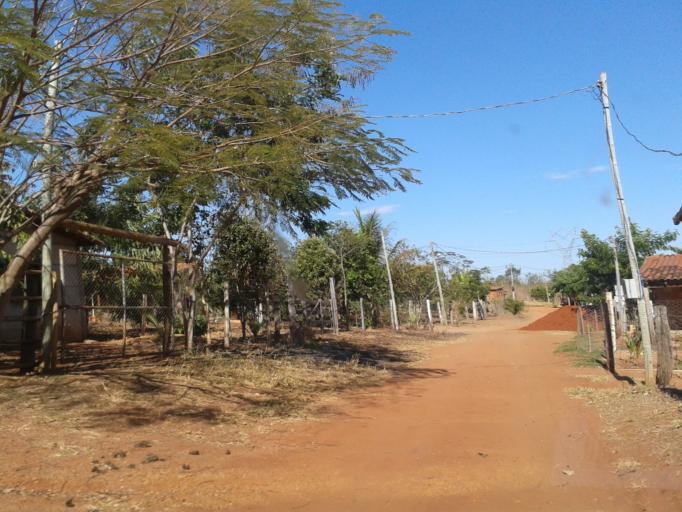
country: BR
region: Minas Gerais
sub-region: Santa Vitoria
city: Santa Vitoria
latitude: -19.0061
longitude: -50.3266
